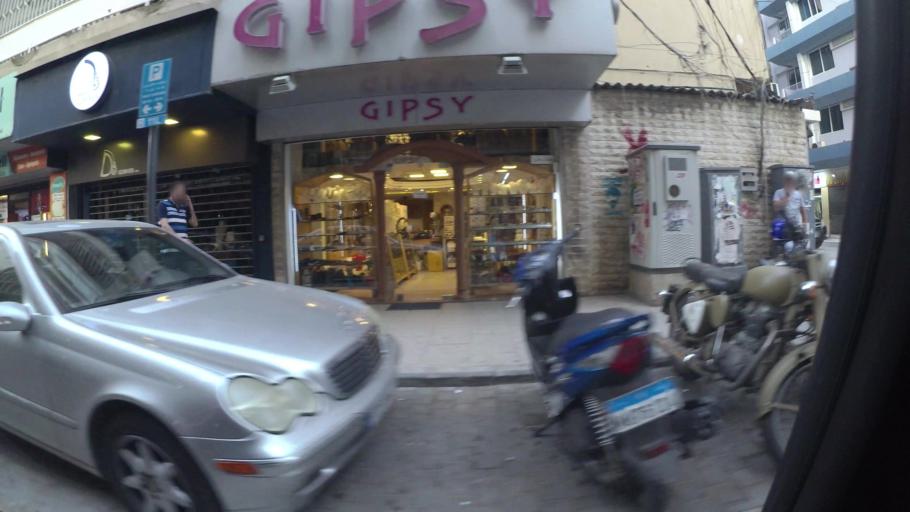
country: LB
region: Beyrouth
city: Ra's Bayrut
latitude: 33.8968
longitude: 35.4814
